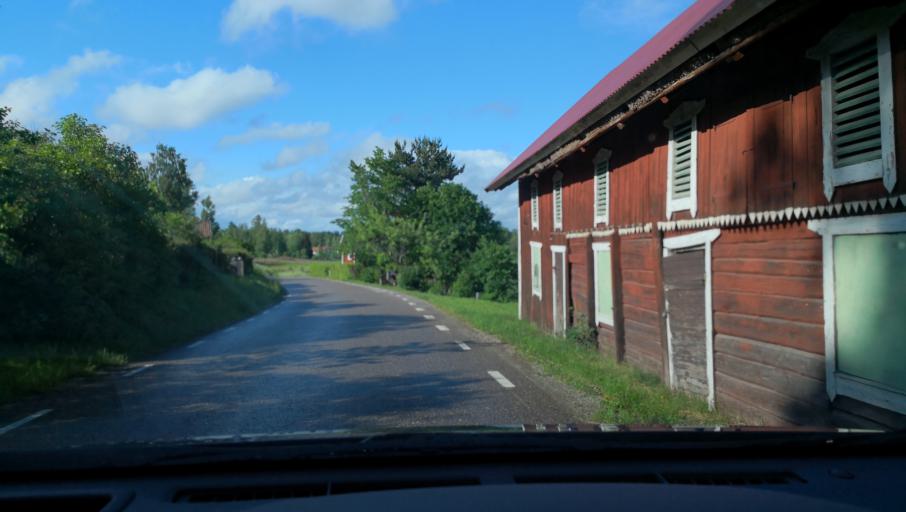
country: SE
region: OErebro
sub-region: Lindesbergs Kommun
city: Fellingsbro
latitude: 59.3221
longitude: 15.6779
